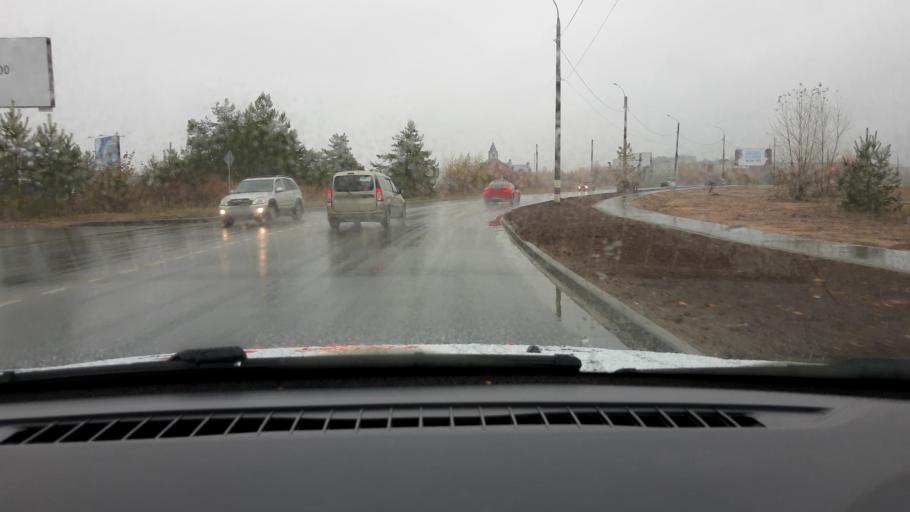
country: RU
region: Nizjnij Novgorod
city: Dzerzhinsk
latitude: 56.2389
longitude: 43.4066
